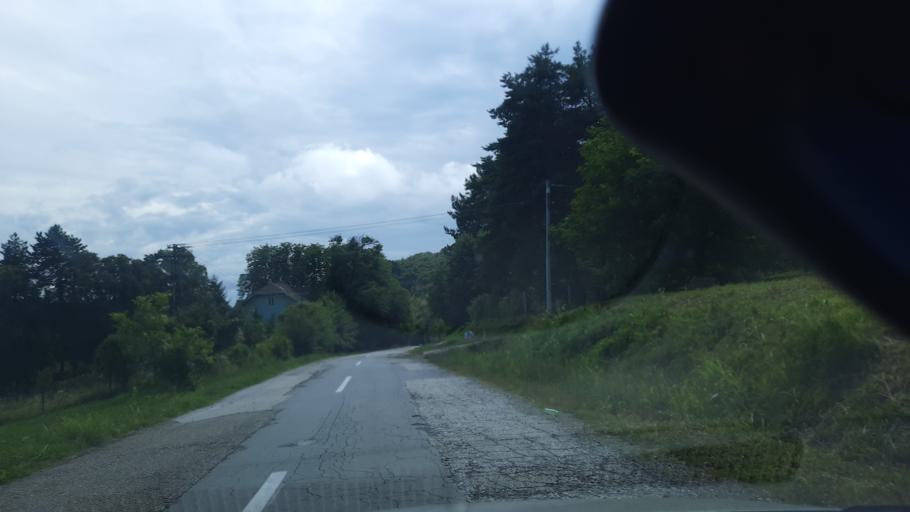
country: RS
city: Glozan
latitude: 45.1346
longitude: 19.5785
